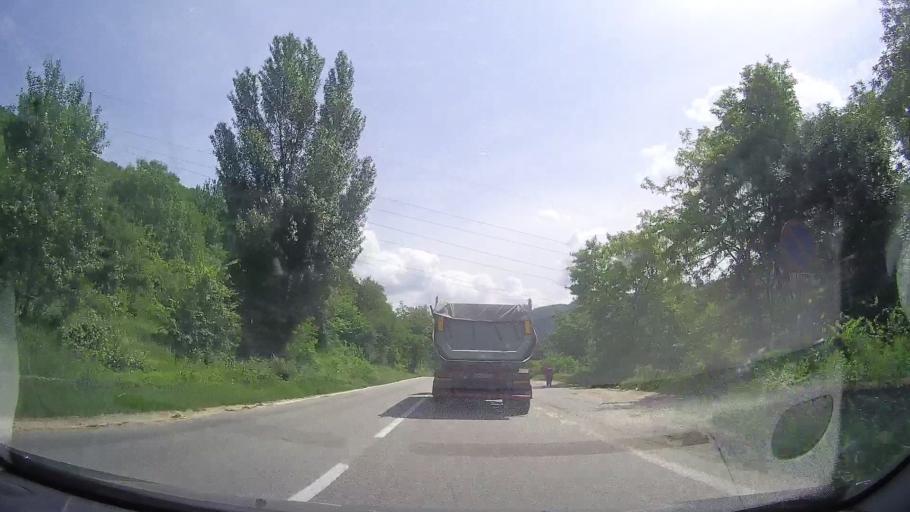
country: RO
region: Valcea
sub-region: Oras Calimanesti
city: Calimanesti
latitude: 45.2770
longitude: 24.3143
